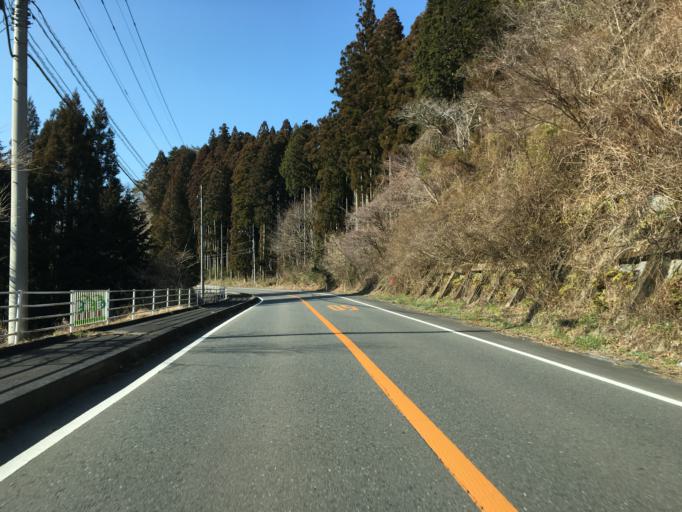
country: JP
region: Ibaraki
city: Takahagi
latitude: 36.7414
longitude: 140.6058
